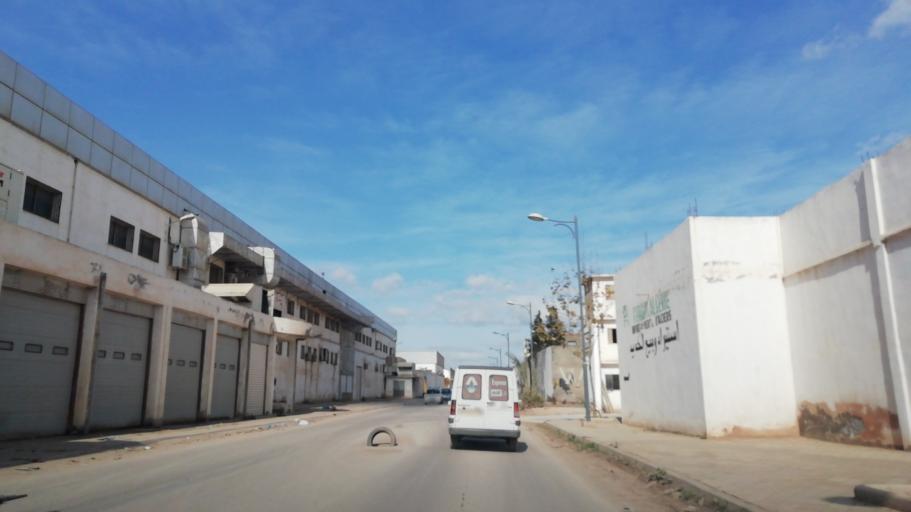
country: DZ
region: Oran
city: Es Senia
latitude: 35.6420
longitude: -0.5883
